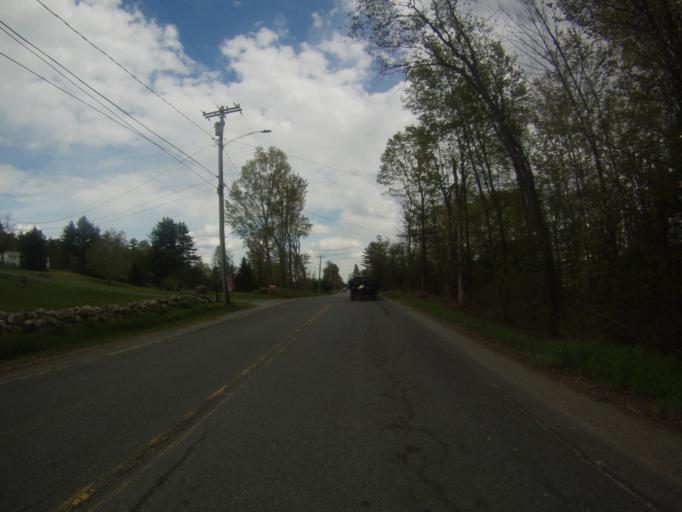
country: US
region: New York
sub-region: Essex County
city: Mineville
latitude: 44.0694
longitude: -73.5199
